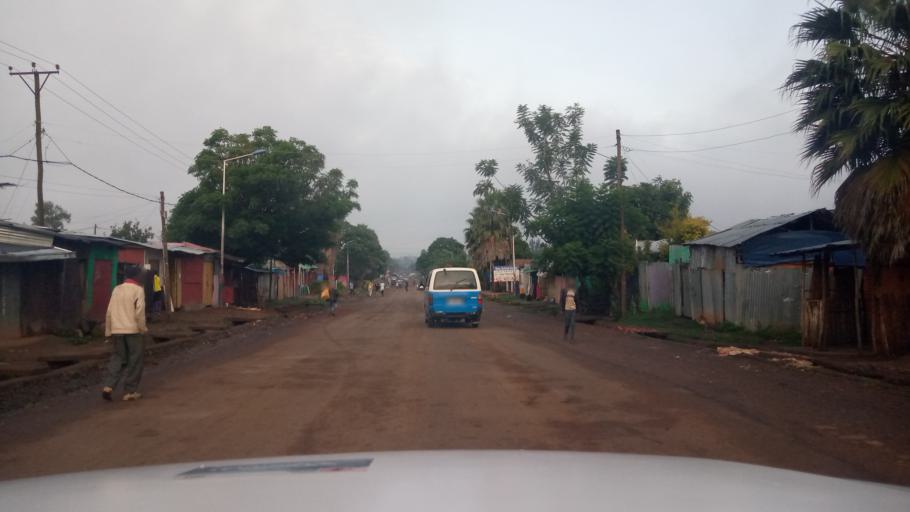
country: ET
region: Oromiya
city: Jima
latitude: 7.6845
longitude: 36.8478
